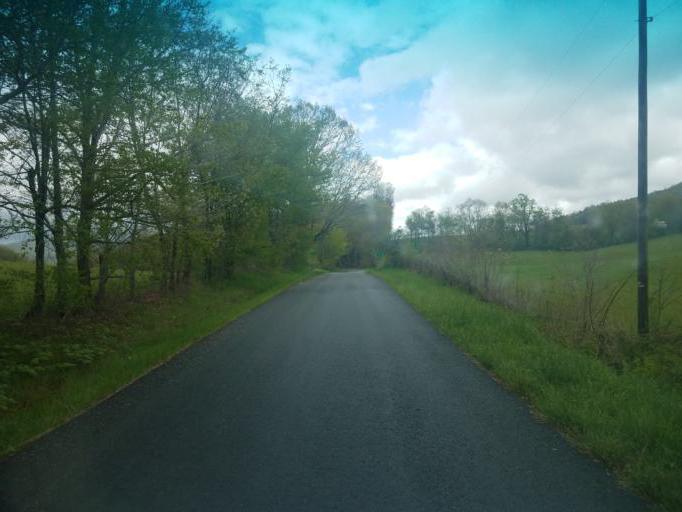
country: US
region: Virginia
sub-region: Smyth County
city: Atkins
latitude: 36.9637
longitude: -81.3920
